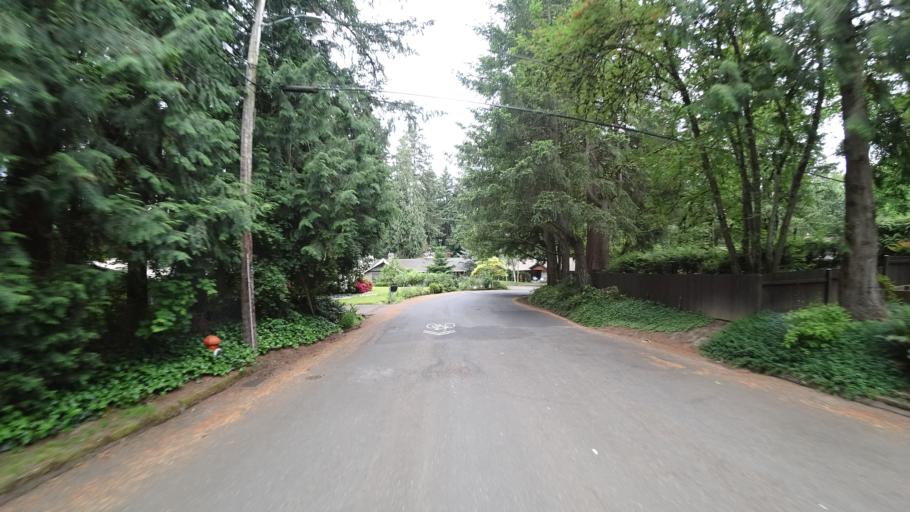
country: US
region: Oregon
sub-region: Washington County
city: Garden Home-Whitford
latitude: 45.4716
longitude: -122.7411
